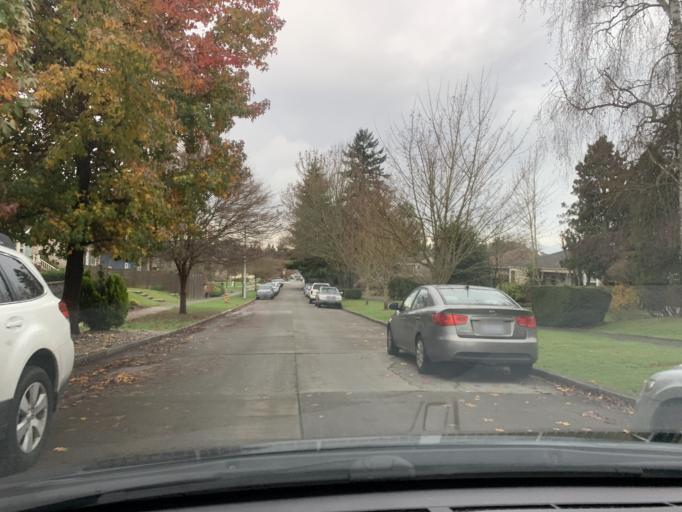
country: US
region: Washington
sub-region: King County
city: White Center
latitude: 47.5625
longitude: -122.3935
